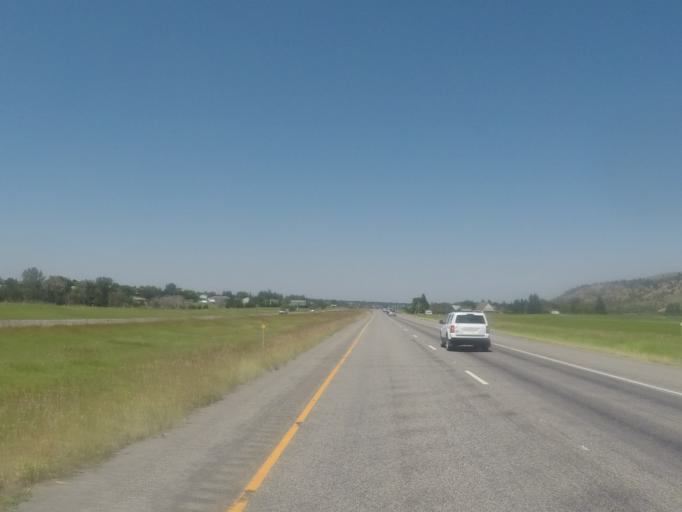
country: US
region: Montana
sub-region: Gallatin County
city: Bozeman
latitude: 45.6653
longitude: -110.9760
